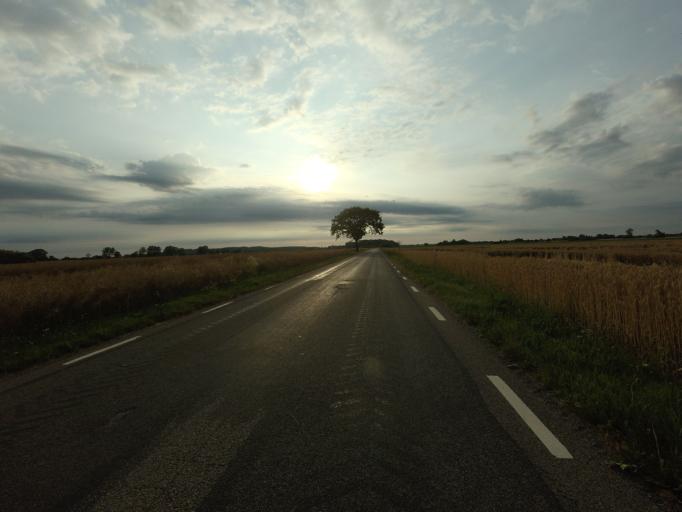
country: SE
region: Skane
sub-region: Helsingborg
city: Odakra
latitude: 56.1496
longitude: 12.6619
